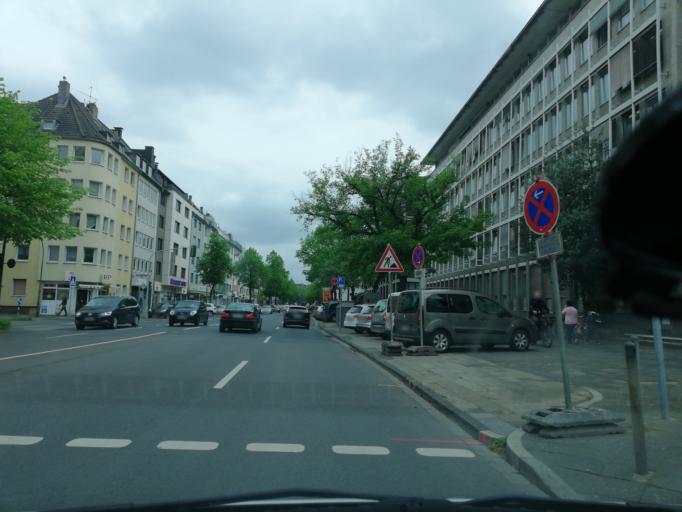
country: DE
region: North Rhine-Westphalia
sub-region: Regierungsbezirk Dusseldorf
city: Dusseldorf
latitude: 51.2459
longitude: 6.7791
